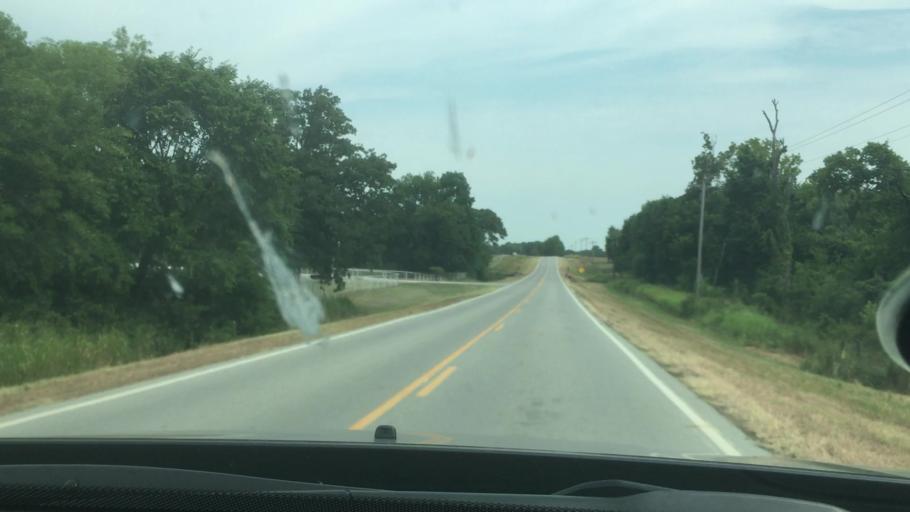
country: US
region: Oklahoma
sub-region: Coal County
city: Coalgate
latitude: 34.5715
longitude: -96.4068
